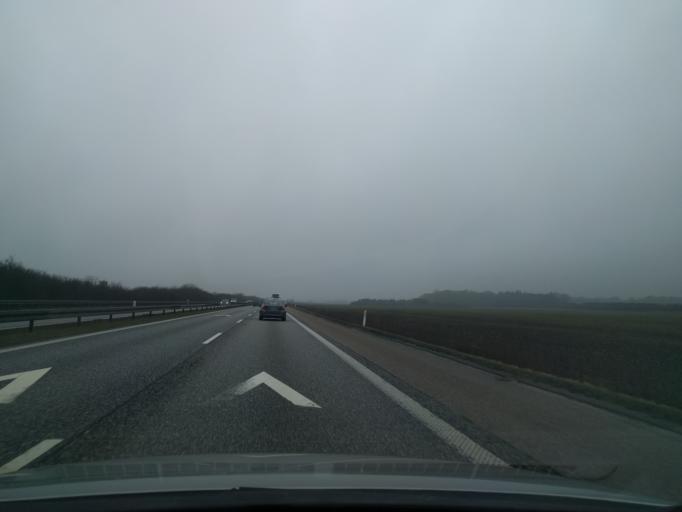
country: DK
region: Zealand
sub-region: Ringsted Kommune
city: Ringsted
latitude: 55.4516
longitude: 11.6801
